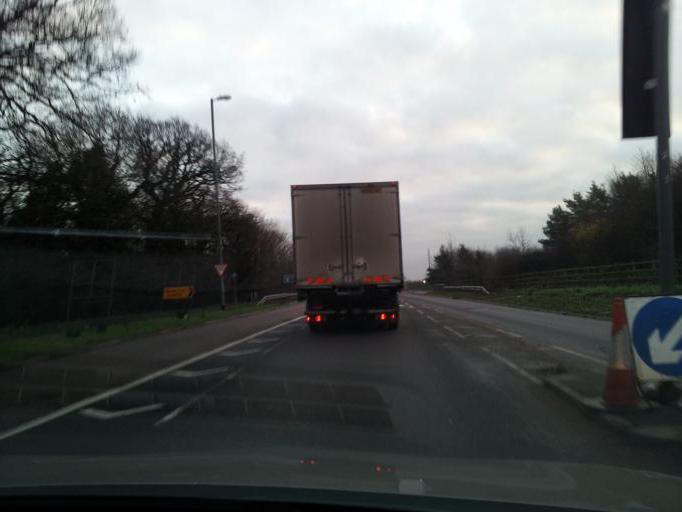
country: GB
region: England
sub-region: Cambridgeshire
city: Girton
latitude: 52.2146
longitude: 0.0765
